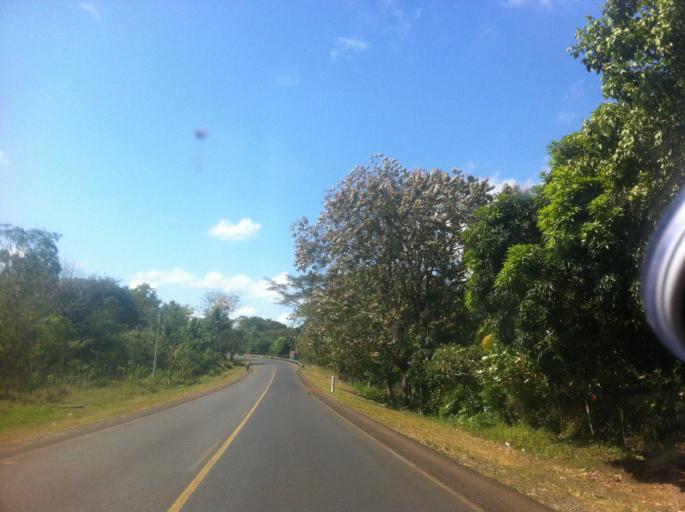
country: NI
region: Rio San Juan
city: San Carlos
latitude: 11.1890
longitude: -84.7446
